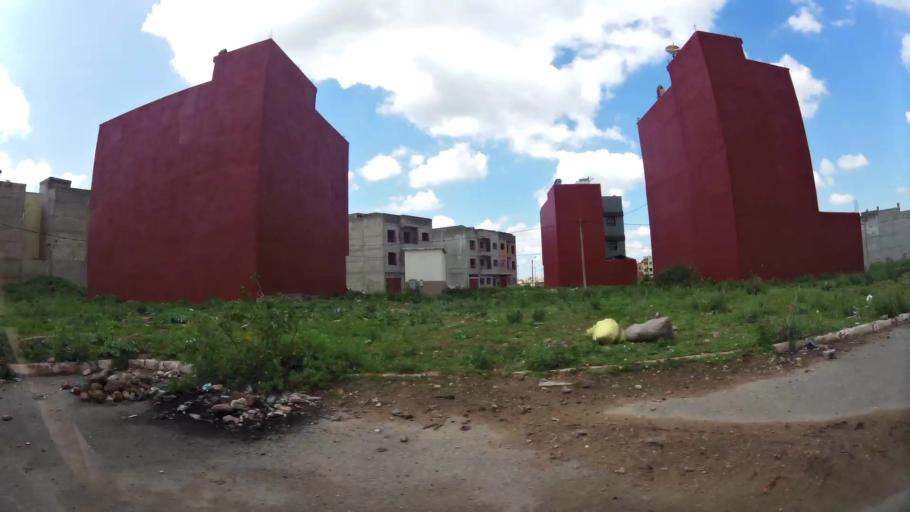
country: MA
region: Chaouia-Ouardigha
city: Nouaseur
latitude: 33.3628
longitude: -7.5335
